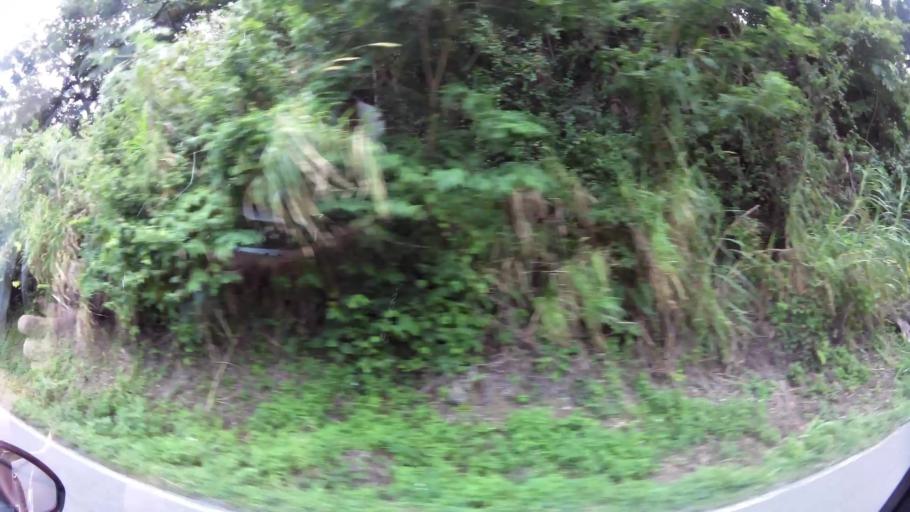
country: TT
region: Diego Martin
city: Petit Valley
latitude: 10.7277
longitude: -61.4940
